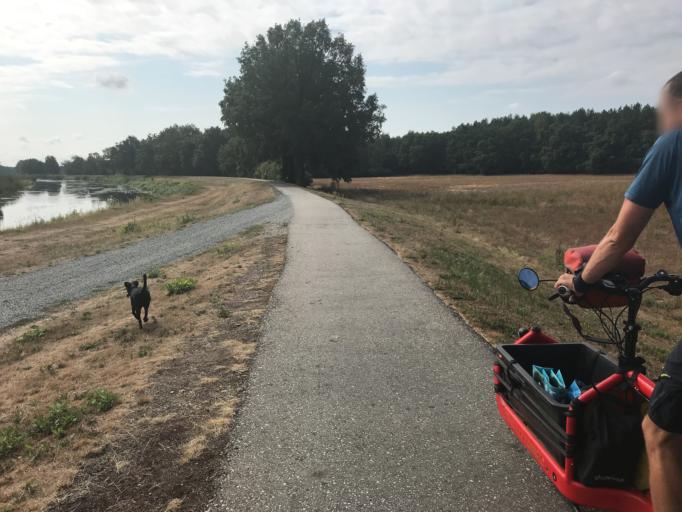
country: DE
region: Brandenburg
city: Schilda
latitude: 51.5871
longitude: 13.3319
